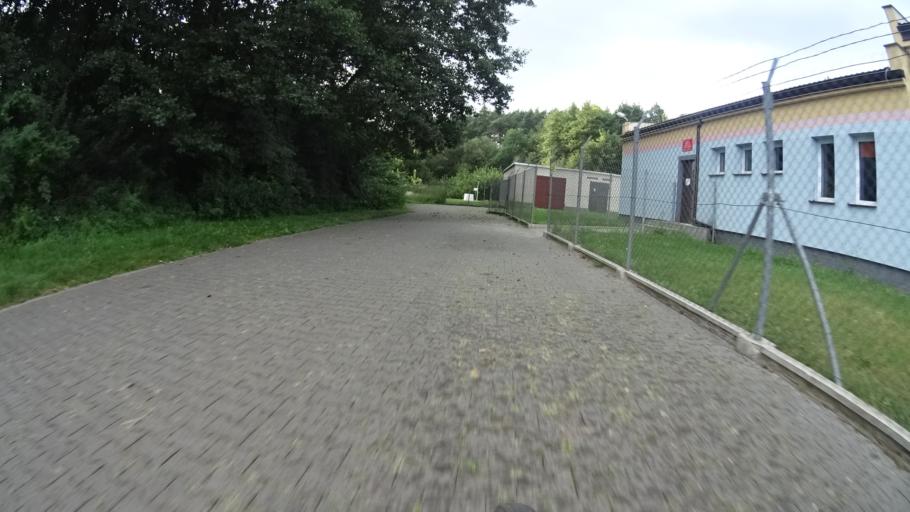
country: PL
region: Masovian Voivodeship
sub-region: Powiat grojecki
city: Mogielnica
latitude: 51.6989
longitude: 20.7235
